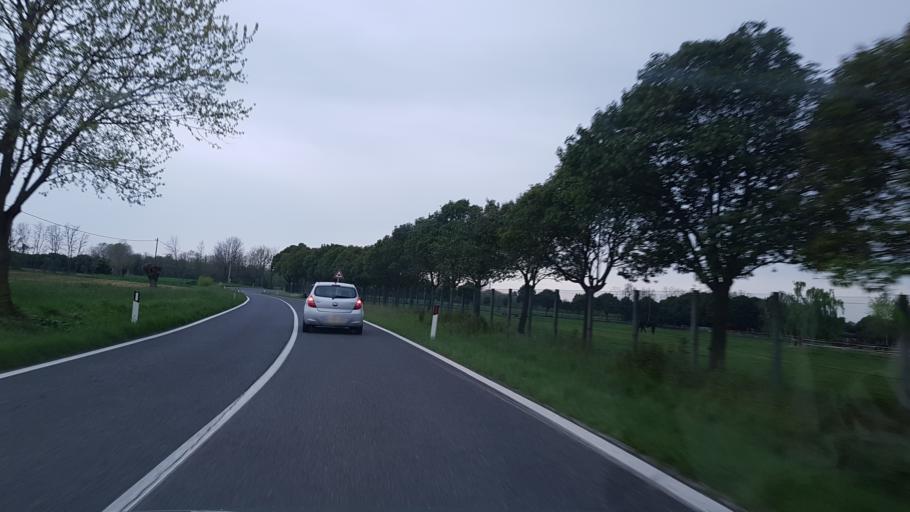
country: IT
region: Friuli Venezia Giulia
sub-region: Provincia di Udine
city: Sottoselva
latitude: 45.8986
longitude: 13.3259
